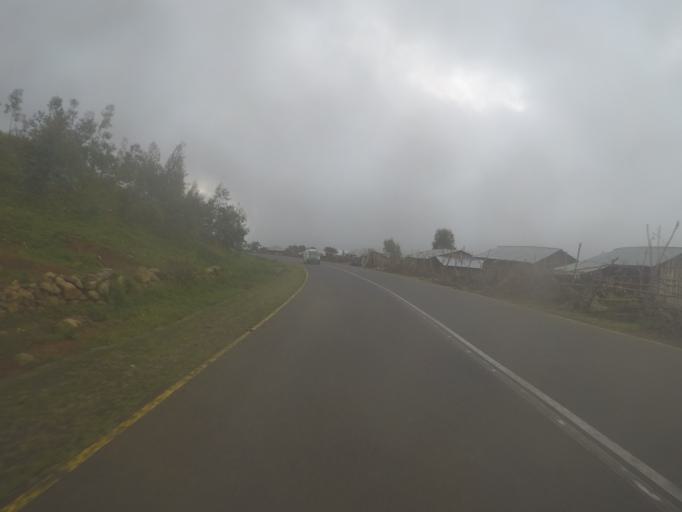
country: ET
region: Amhara
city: Gondar
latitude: 12.7329
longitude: 37.5175
